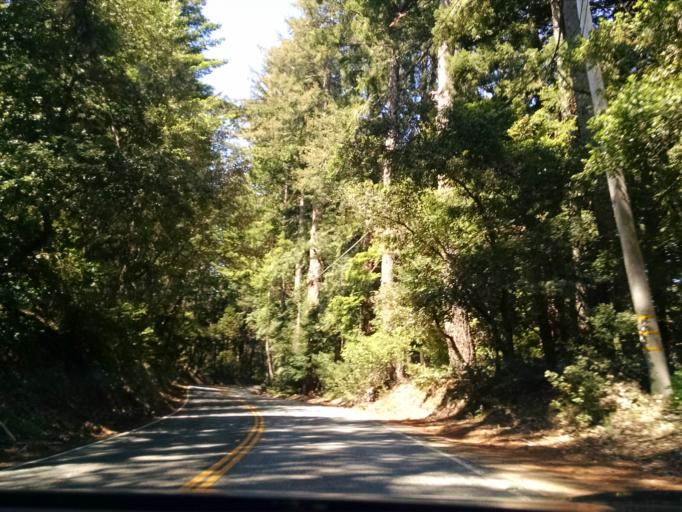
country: US
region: California
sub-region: San Mateo County
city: Woodside
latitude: 37.4135
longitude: -122.3088
